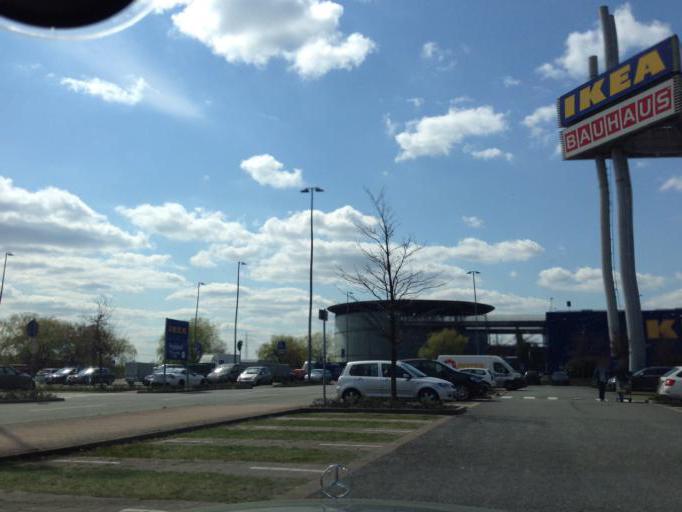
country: DE
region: Hamburg
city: Wandsbek
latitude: 53.5110
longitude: 10.0958
